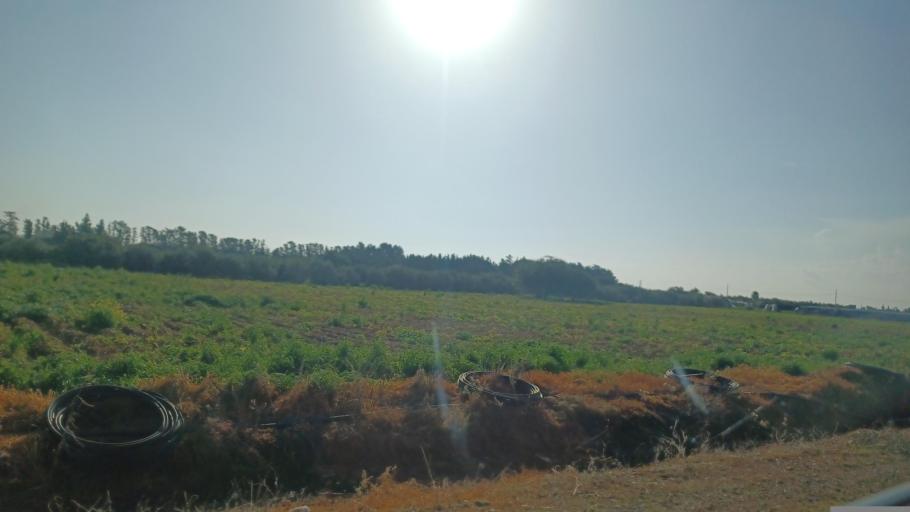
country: CY
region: Pafos
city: Paphos
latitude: 34.7117
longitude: 32.5274
